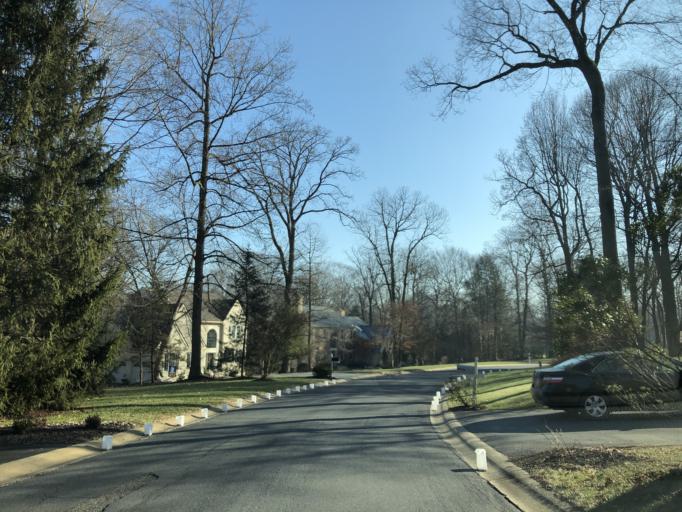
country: US
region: Pennsylvania
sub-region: Chester County
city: Downingtown
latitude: 39.9883
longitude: -75.6997
